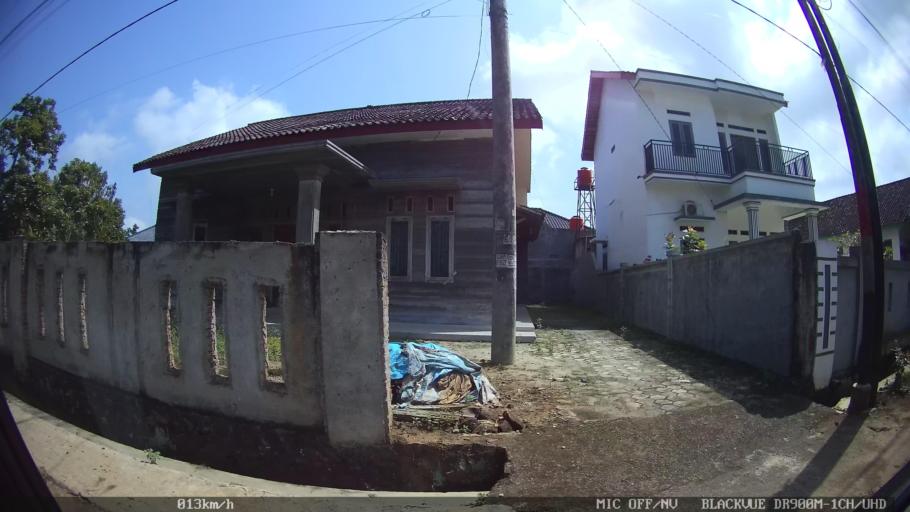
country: ID
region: Lampung
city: Kedaton
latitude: -5.3451
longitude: 105.2941
